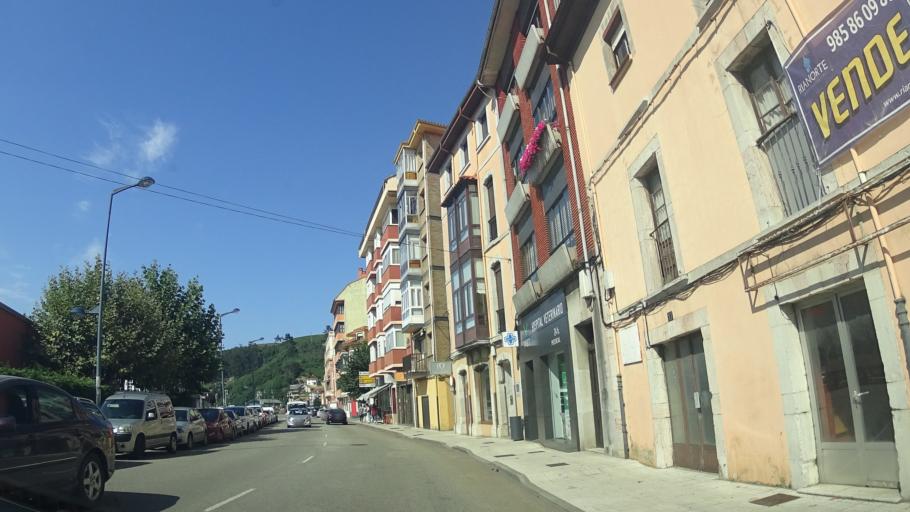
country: ES
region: Asturias
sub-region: Province of Asturias
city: Ribadesella
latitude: 43.4602
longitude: -5.0607
